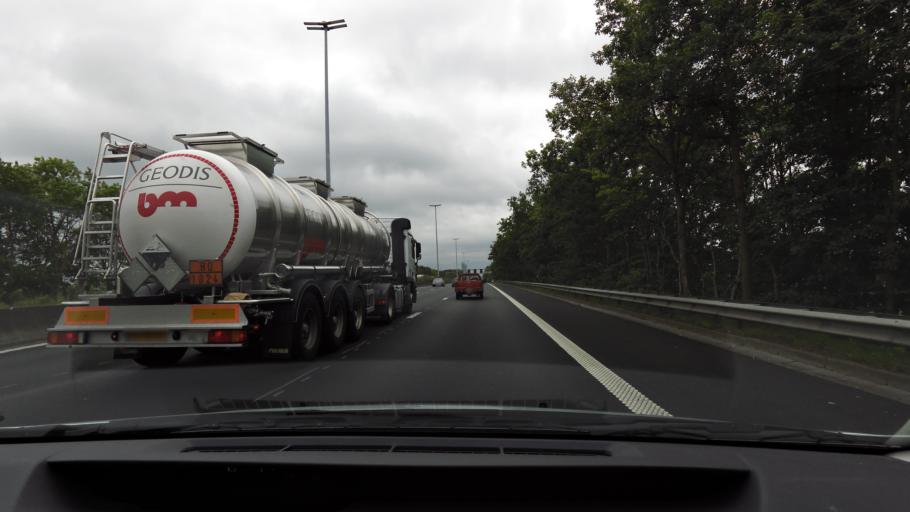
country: BE
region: Flanders
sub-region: Provincie Oost-Vlaanderen
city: Sint-Martens-Latem
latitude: 51.0314
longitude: 3.6480
